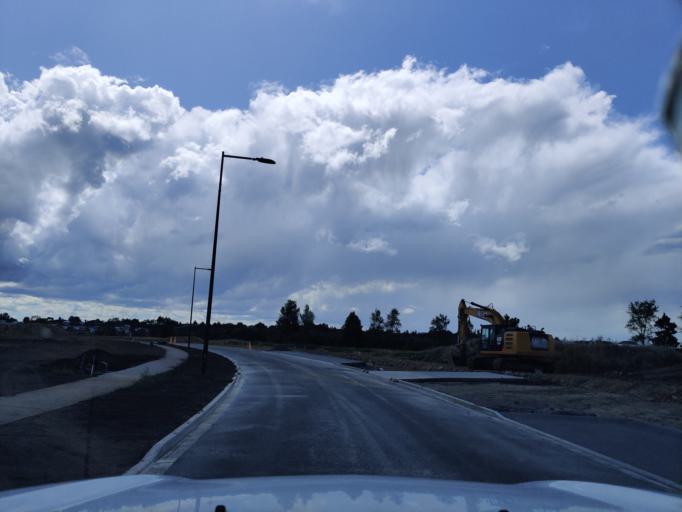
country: NZ
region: Waikato
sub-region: Waikato District
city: Te Kauwhata
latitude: -37.4109
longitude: 175.1532
